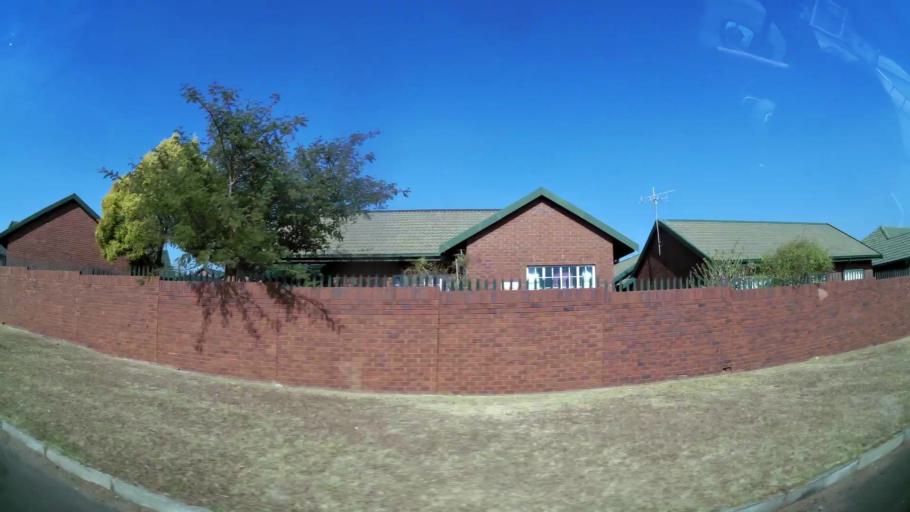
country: ZA
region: Gauteng
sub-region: West Rand District Municipality
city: Randfontein
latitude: -26.1557
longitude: 27.6989
